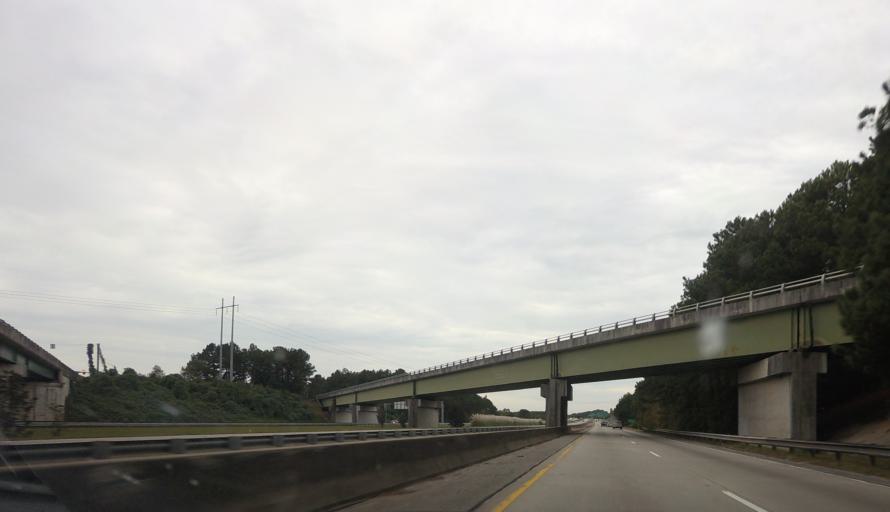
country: US
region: Alabama
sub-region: Russell County
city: Phenix City
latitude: 32.5486
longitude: -84.9515
